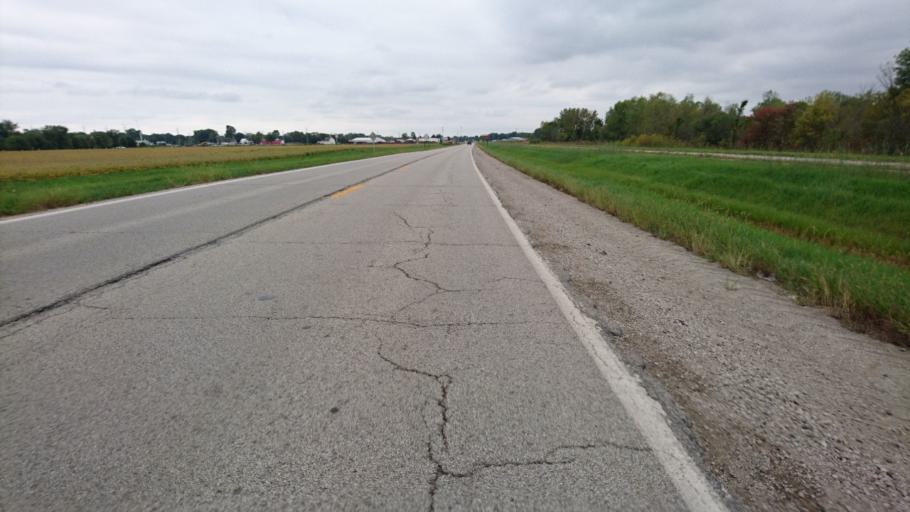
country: US
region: Illinois
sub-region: Livingston County
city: Pontiac
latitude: 40.8982
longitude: -88.6247
